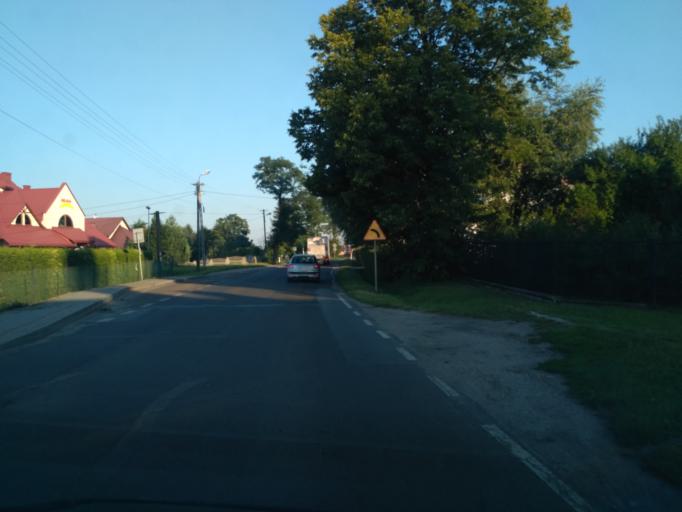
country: PL
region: Subcarpathian Voivodeship
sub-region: Powiat krosnienski
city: Korczyna
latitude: 49.7168
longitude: 21.8000
